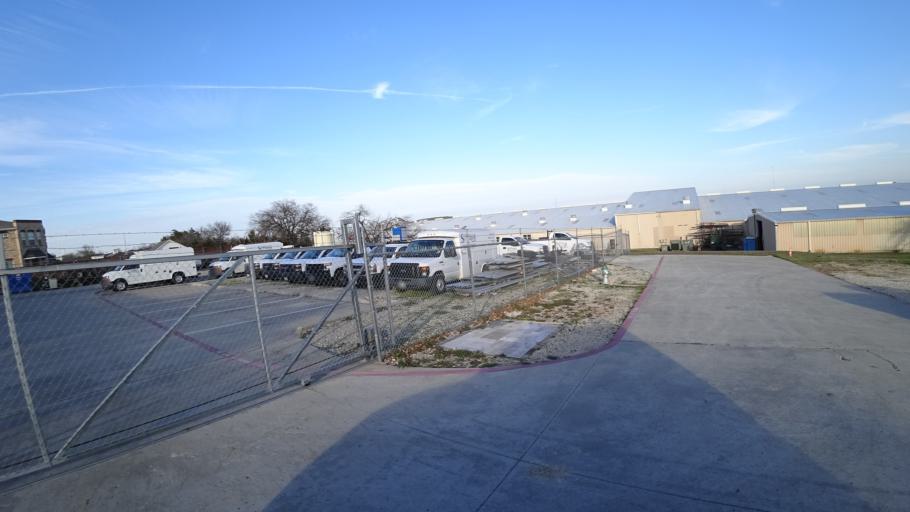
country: US
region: Texas
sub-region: Denton County
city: Lewisville
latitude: 33.0431
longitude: -96.9911
